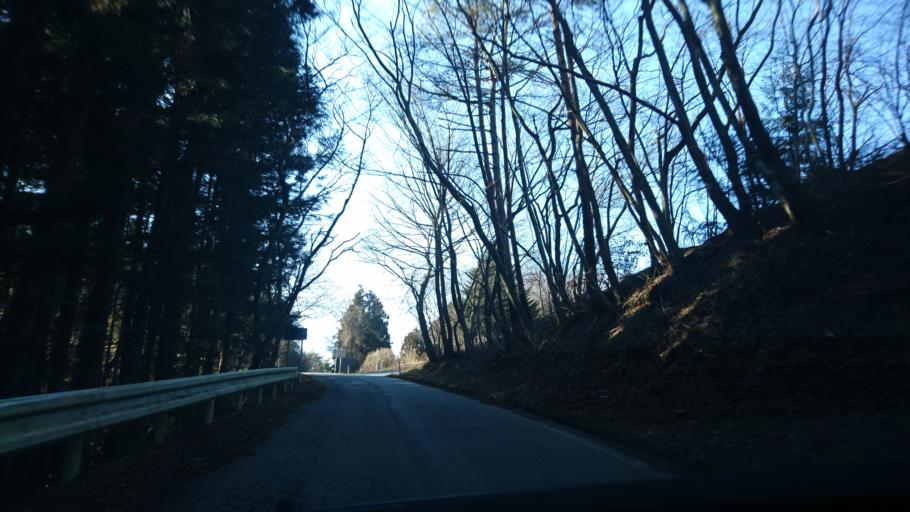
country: JP
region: Iwate
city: Ichinoseki
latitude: 38.8134
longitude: 141.2728
